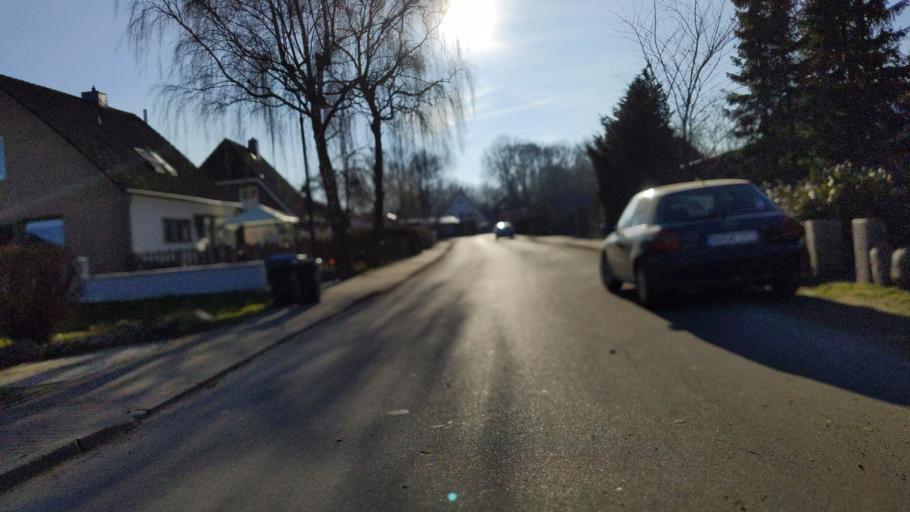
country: DE
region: Schleswig-Holstein
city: Ahrensbok
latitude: 54.0168
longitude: 10.6452
